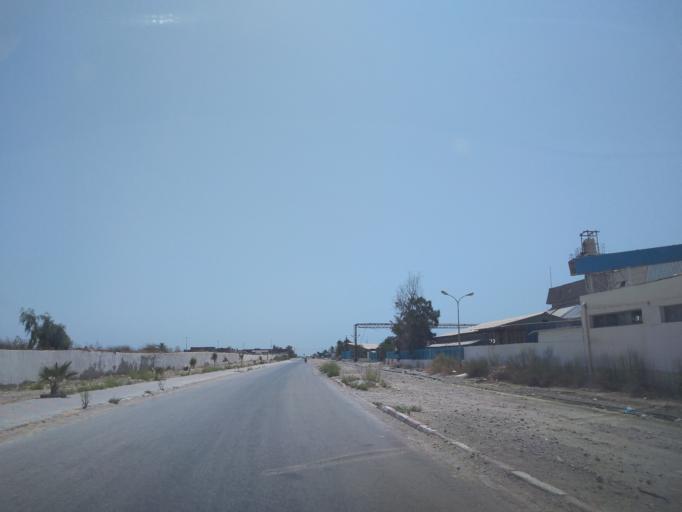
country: TN
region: Safaqis
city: Sfax
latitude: 34.7319
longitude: 10.7764
